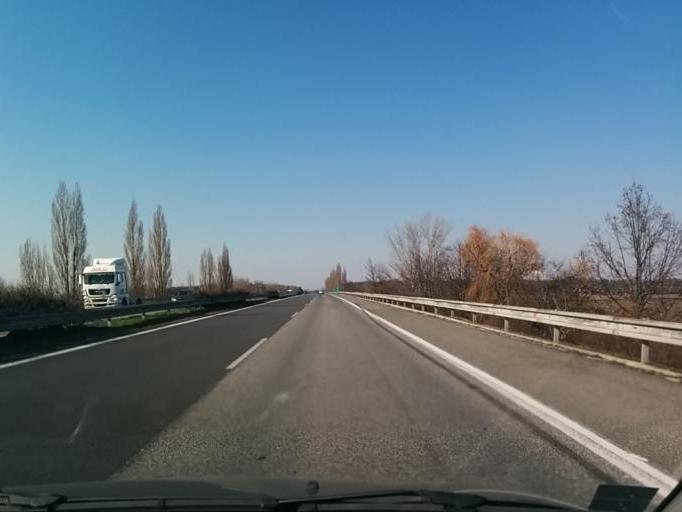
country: SK
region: Trnavsky
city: Leopoldov
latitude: 48.4207
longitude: 17.7461
